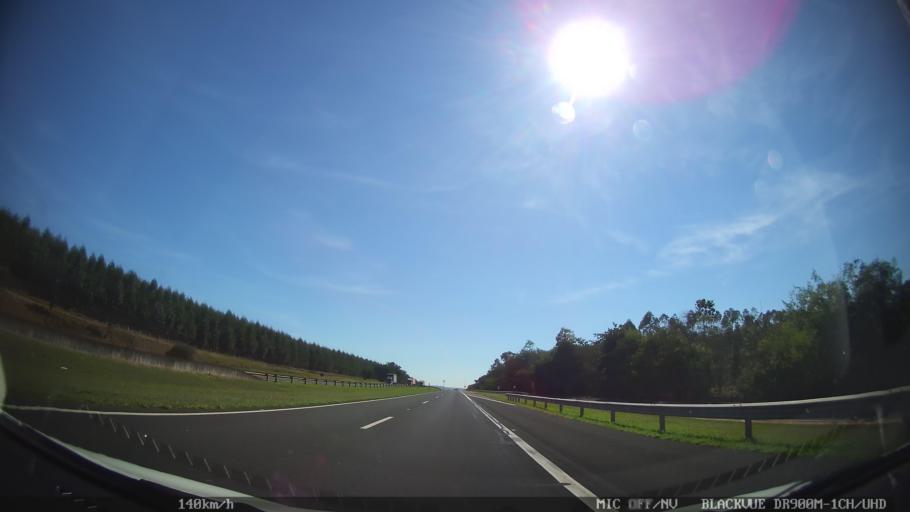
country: BR
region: Sao Paulo
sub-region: Sao Simao
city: Sao Simao
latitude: -21.6091
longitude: -47.6178
